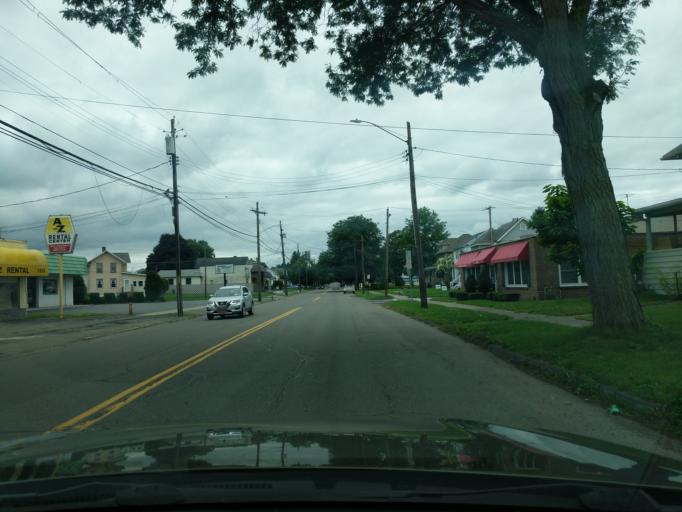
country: US
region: New York
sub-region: Chemung County
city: Elmira Heights
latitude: 42.1087
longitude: -76.8196
